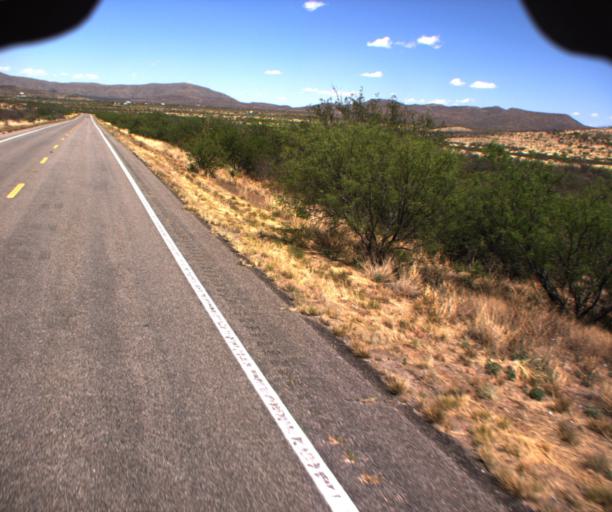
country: US
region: Arizona
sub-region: Cochise County
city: Bisbee
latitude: 31.5306
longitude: -110.0127
